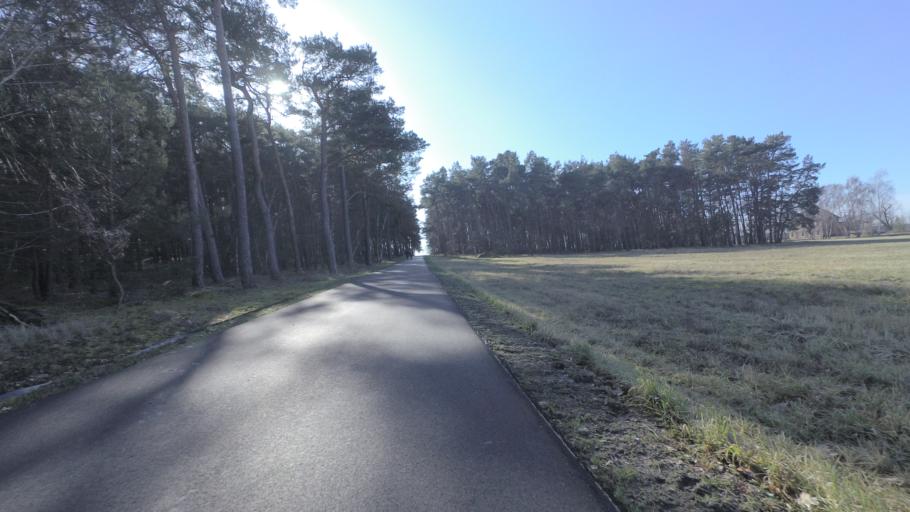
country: DE
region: Brandenburg
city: Juterbog
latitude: 52.0239
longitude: 13.1288
